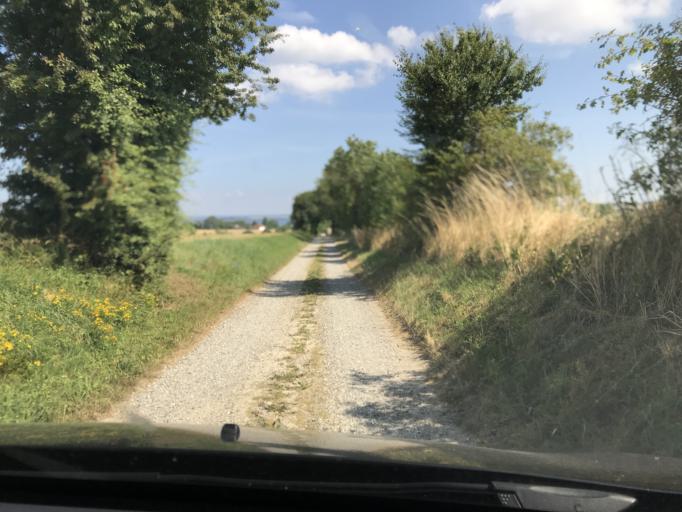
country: DK
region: South Denmark
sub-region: AEro Kommune
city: AEroskobing
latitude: 54.8811
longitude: 10.3610
